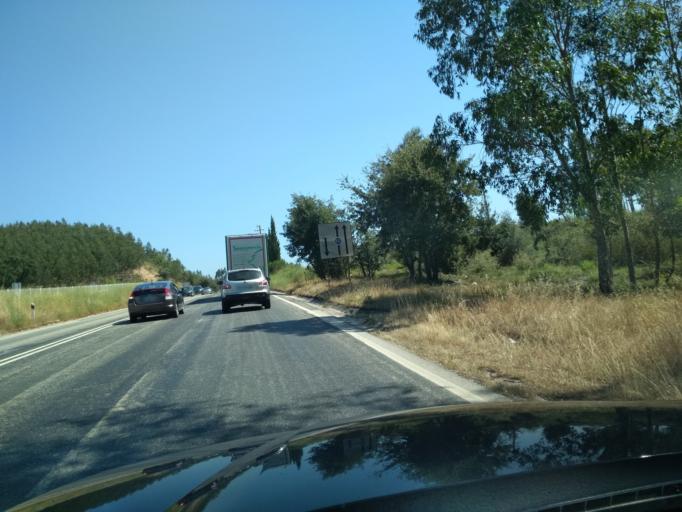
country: PT
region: Coimbra
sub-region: Soure
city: Soure
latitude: 40.0230
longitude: -8.5763
